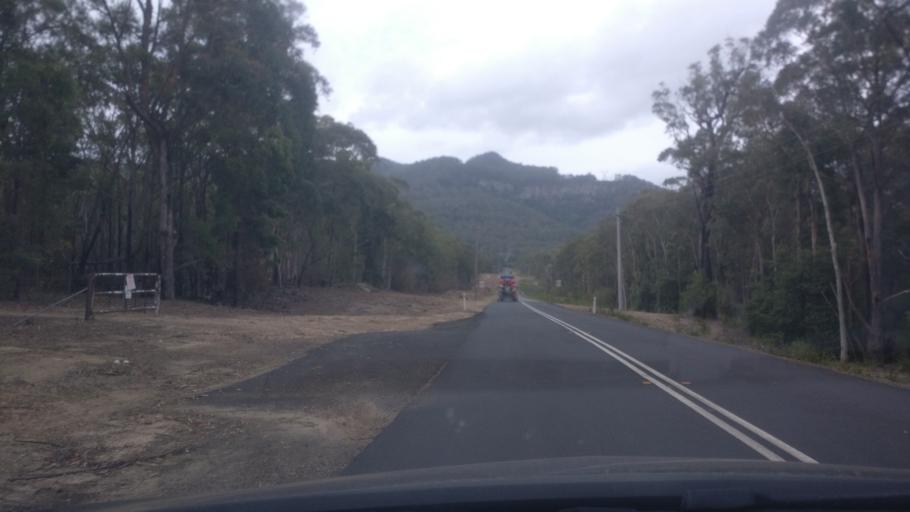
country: AU
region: New South Wales
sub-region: Shoalhaven Shire
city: Kangaroo Valley
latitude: -34.7343
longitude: 150.4794
